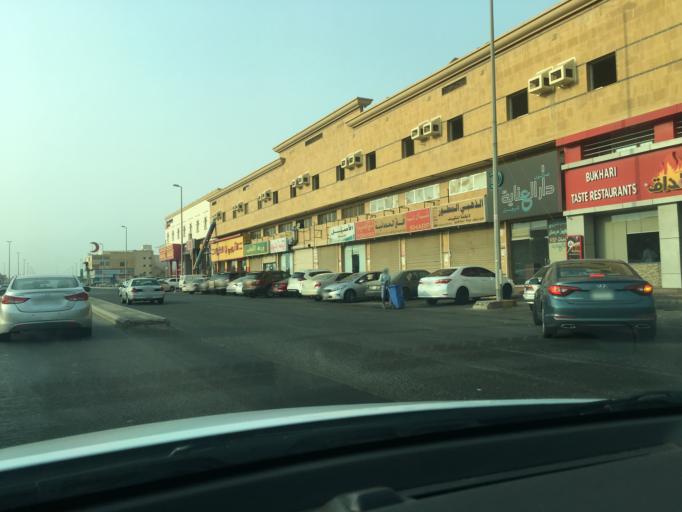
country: SA
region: Makkah
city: Jeddah
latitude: 21.7539
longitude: 39.1866
